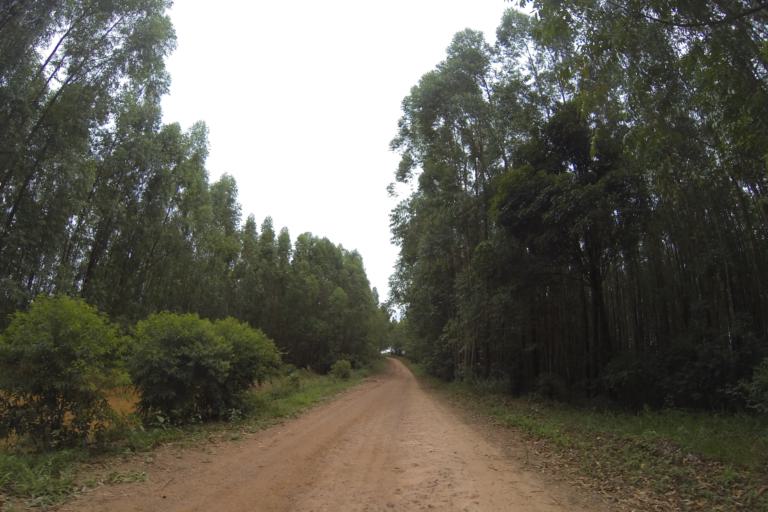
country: BR
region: Minas Gerais
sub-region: Ibia
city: Ibia
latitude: -19.6652
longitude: -46.6966
